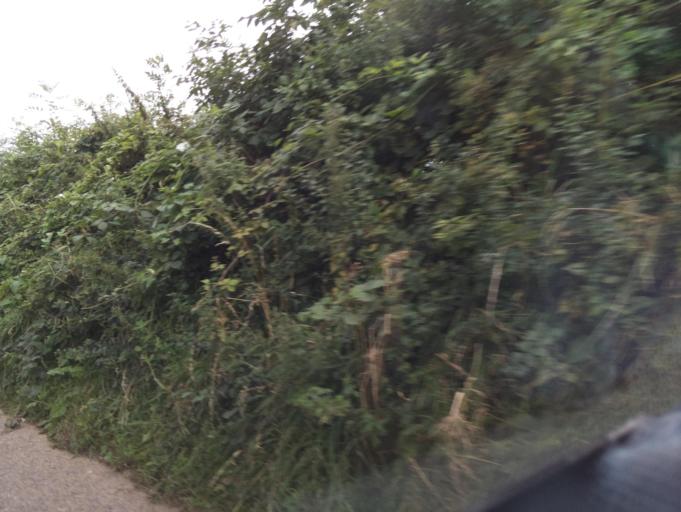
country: GB
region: England
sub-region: Devon
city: South Brent
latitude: 50.3949
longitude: -3.8399
